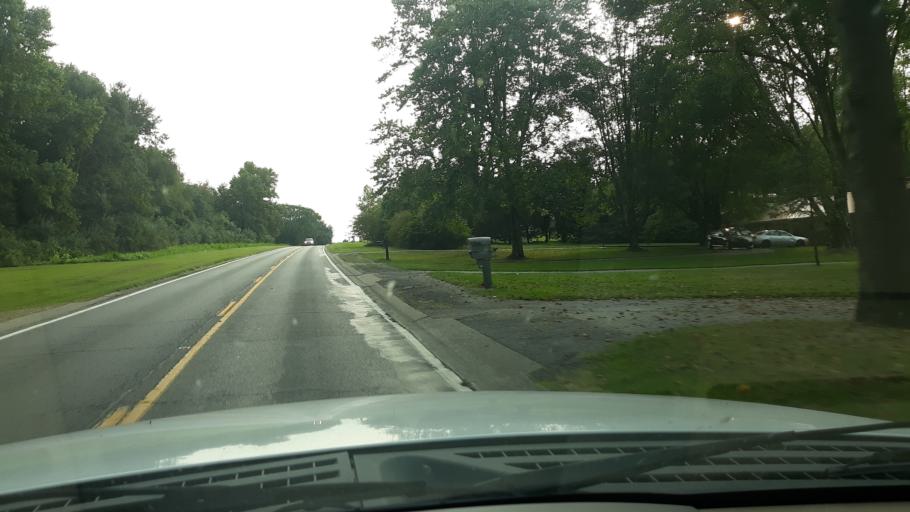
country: US
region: Illinois
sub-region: Wabash County
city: Mount Carmel
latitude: 38.3948
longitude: -87.8028
